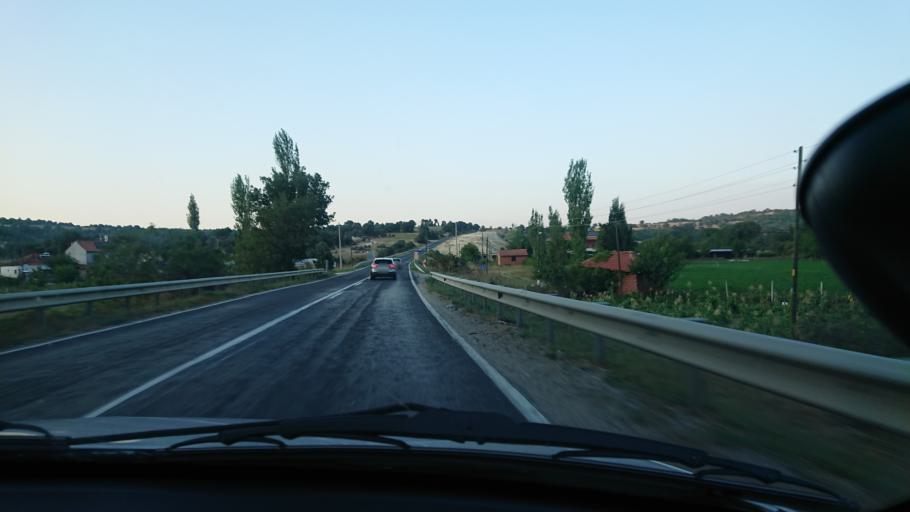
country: TR
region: Usak
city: Gure
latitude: 38.7569
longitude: 29.1978
